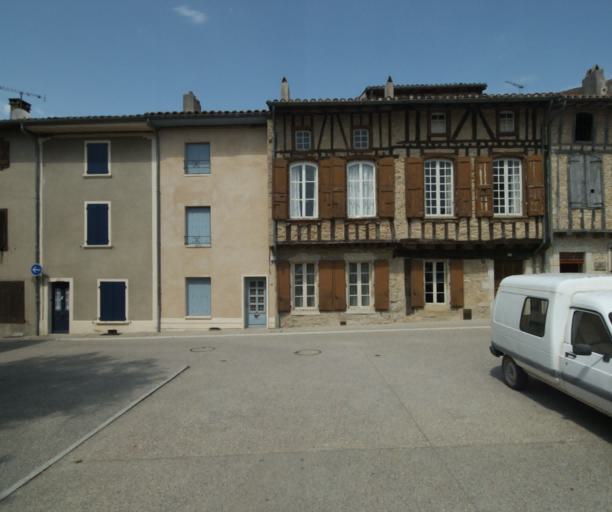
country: FR
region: Midi-Pyrenees
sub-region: Departement de la Haute-Garonne
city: Saint-Felix-Lauragais
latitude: 43.4493
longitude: 1.8877
